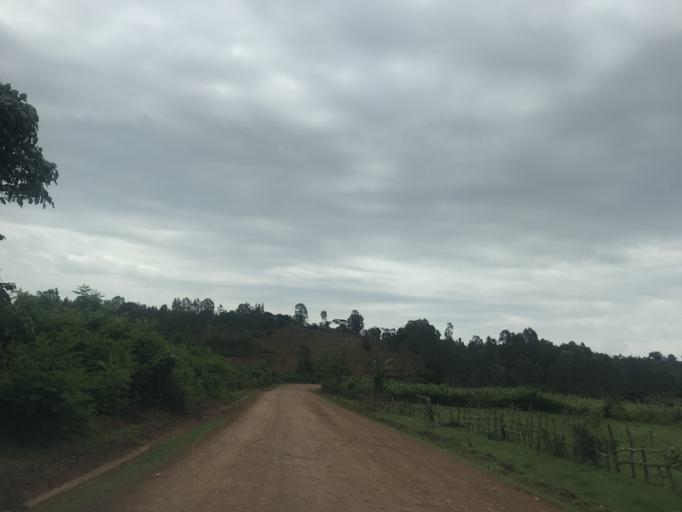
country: ET
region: Oromiya
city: Shambu
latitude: 9.8835
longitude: 36.6496
